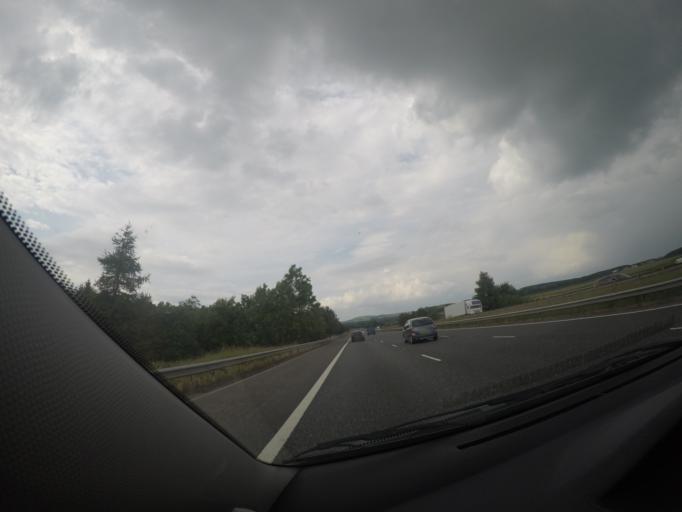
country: GB
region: Scotland
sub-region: Dumfries and Galloway
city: Lockerbie
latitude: 55.0865
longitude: -3.3186
